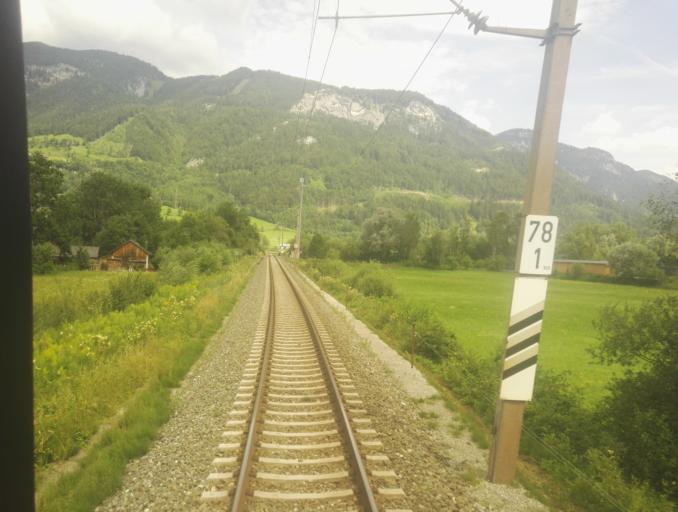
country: AT
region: Styria
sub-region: Politischer Bezirk Liezen
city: Irdning
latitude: 47.5200
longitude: 14.0851
